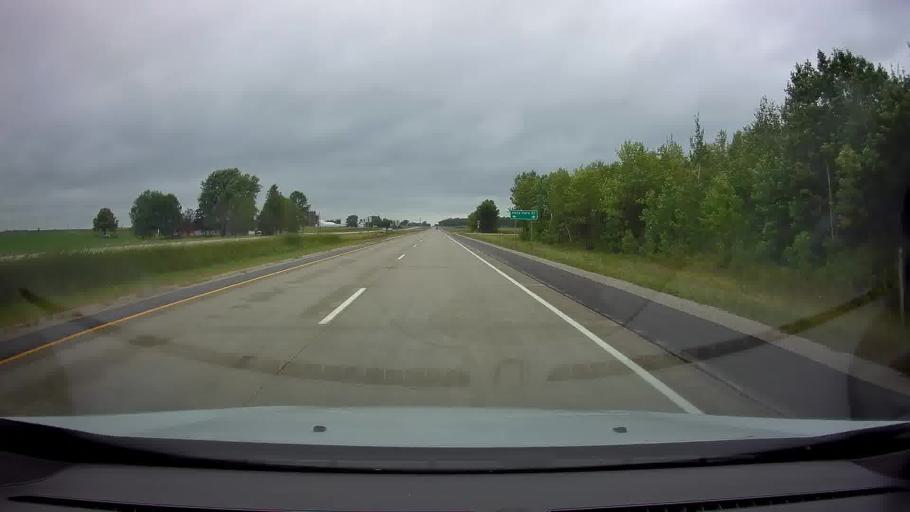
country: US
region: Wisconsin
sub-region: Brown County
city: Pulaski
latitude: 44.6202
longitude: -88.2691
